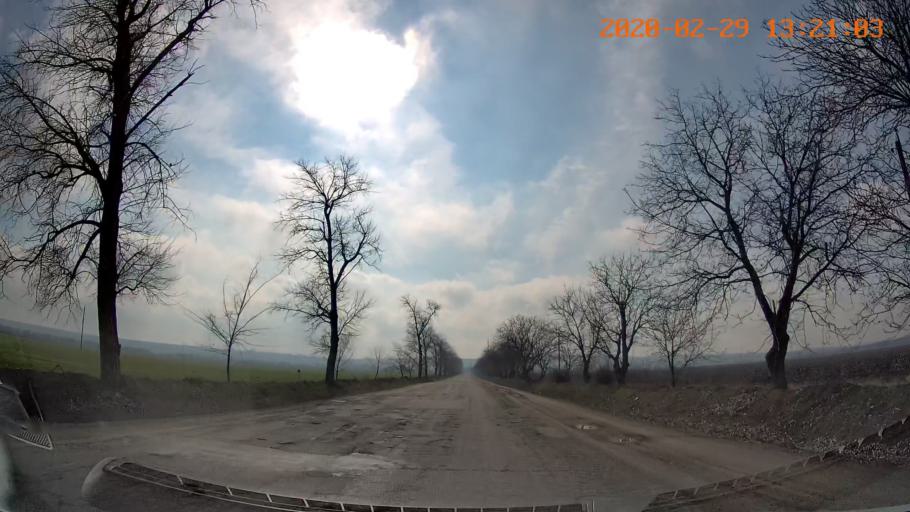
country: MD
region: Telenesti
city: Camenca
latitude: 47.9735
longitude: 28.6362
